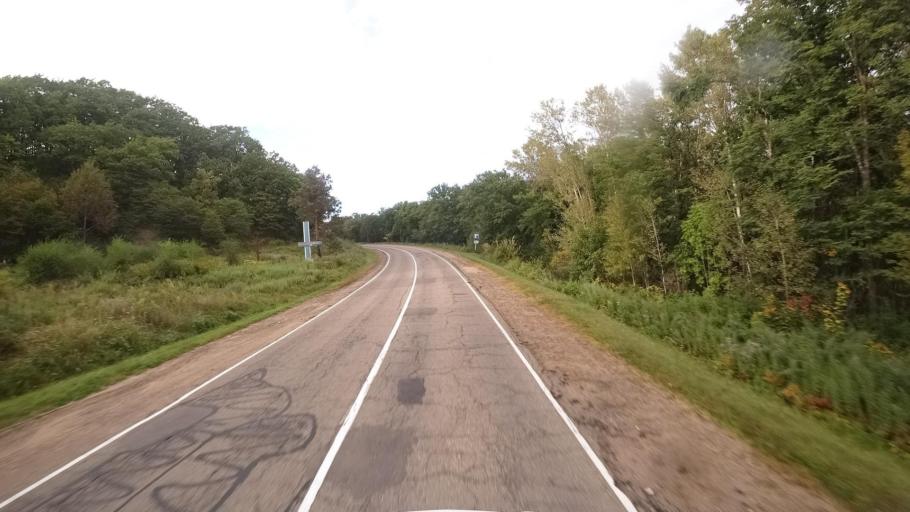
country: RU
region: Primorskiy
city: Yakovlevka
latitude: 44.4075
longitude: 133.4575
